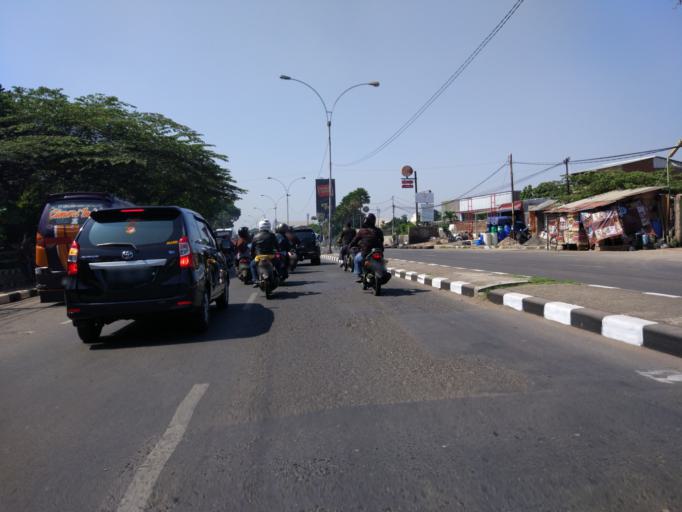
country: ID
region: West Java
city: Margahayukencana
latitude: -6.9440
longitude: 107.5860
